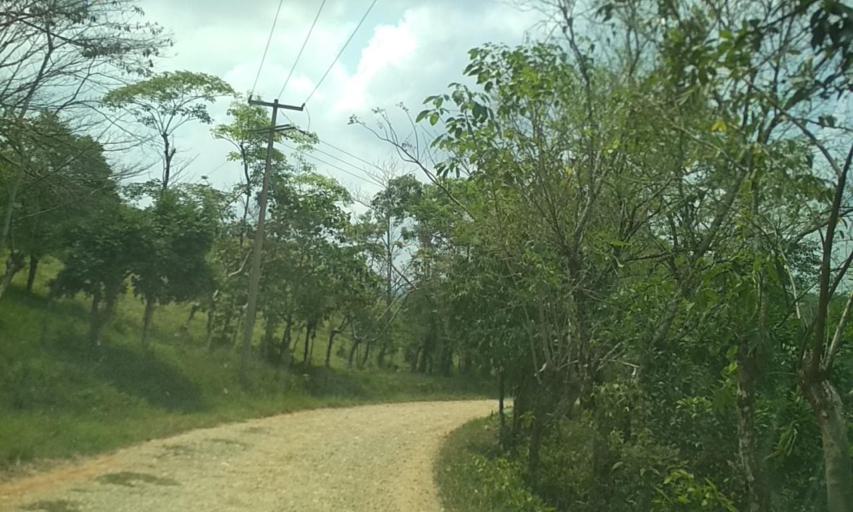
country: MX
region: Tabasco
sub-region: Huimanguillo
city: Francisco Rueda
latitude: 17.5833
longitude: -93.7898
